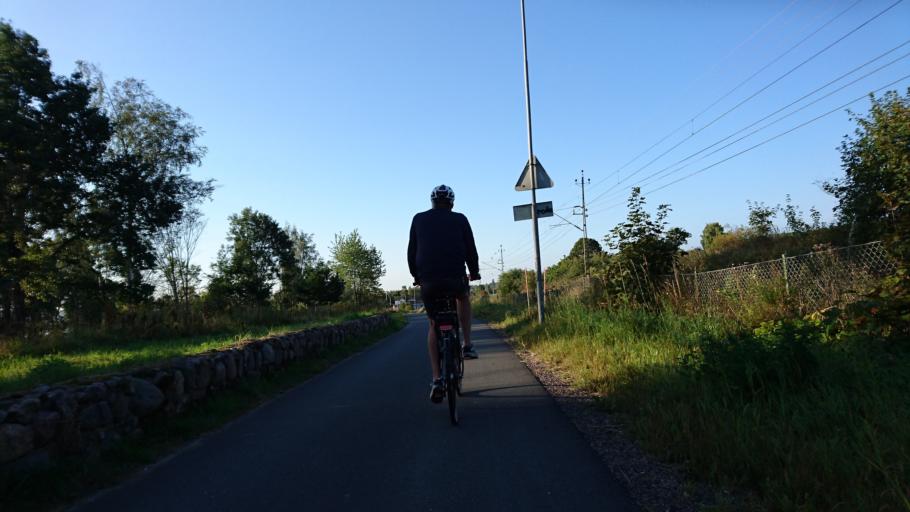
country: SE
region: Joenkoeping
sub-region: Jonkopings Kommun
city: Jonkoping
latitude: 57.8073
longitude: 14.1519
